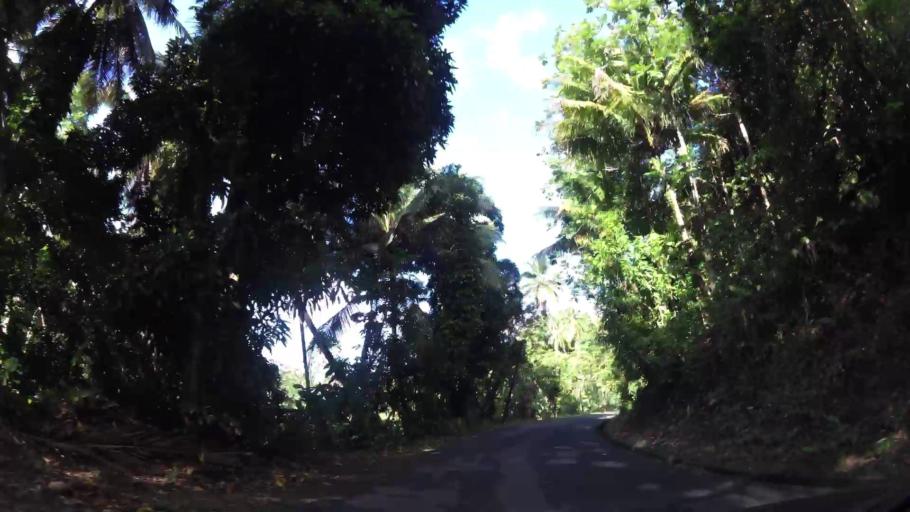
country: DM
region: Saint John
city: Portsmouth
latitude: 15.5745
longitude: -61.4346
